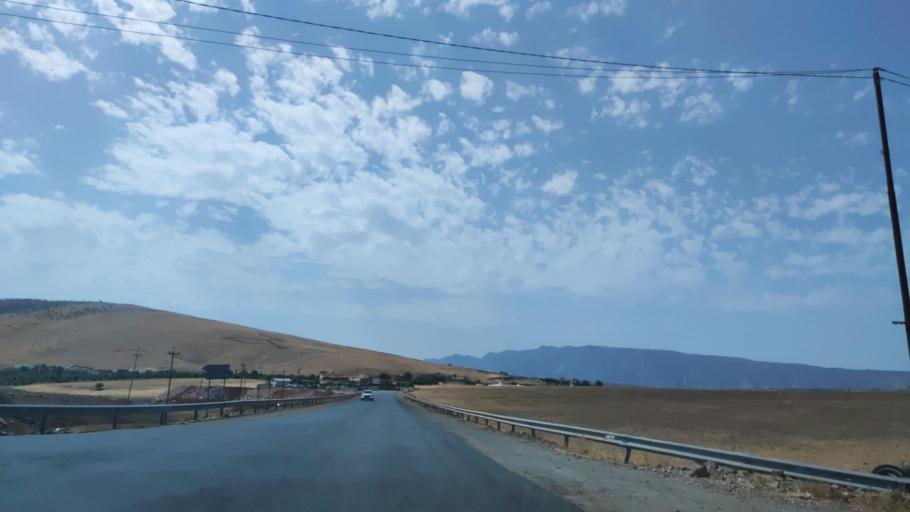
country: IQ
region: Arbil
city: Shaqlawah
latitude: 36.4705
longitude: 44.3973
